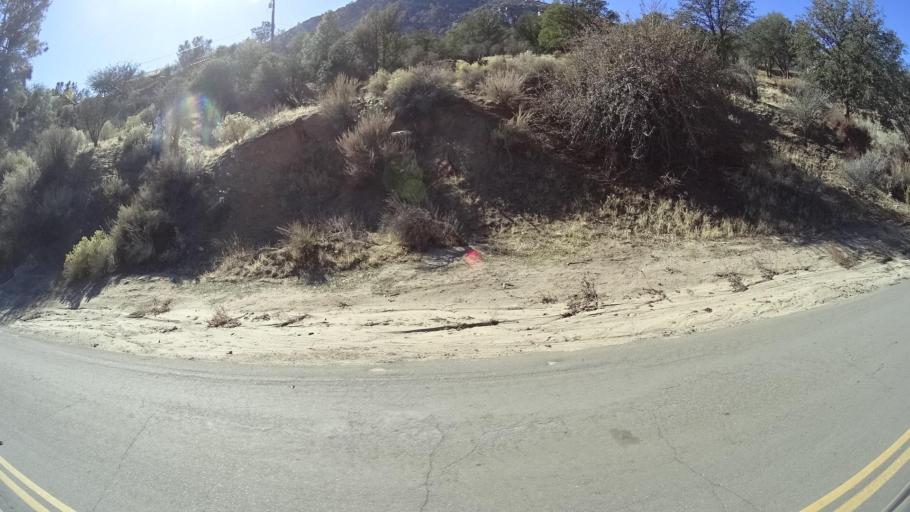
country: US
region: California
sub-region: Kern County
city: Kernville
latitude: 35.7741
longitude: -118.4431
